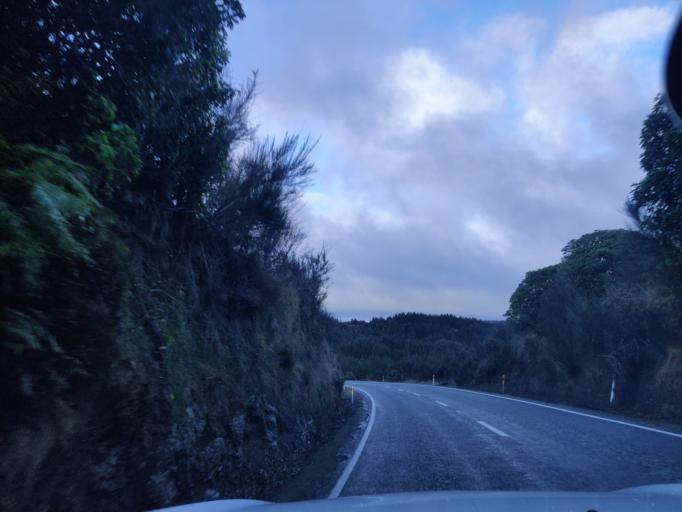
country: NZ
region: Waikato
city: Turangi
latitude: -38.7183
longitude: 175.6563
